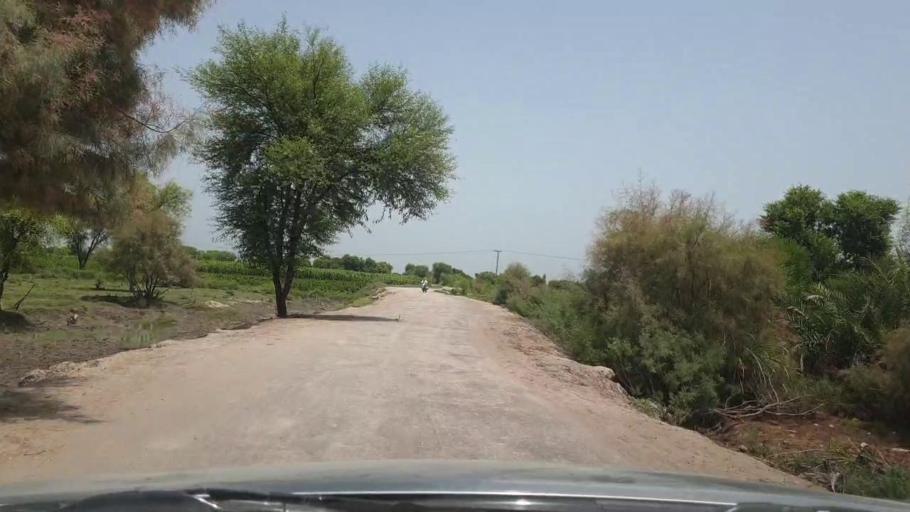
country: PK
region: Sindh
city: Pano Aqil
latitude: 27.8694
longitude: 69.1709
